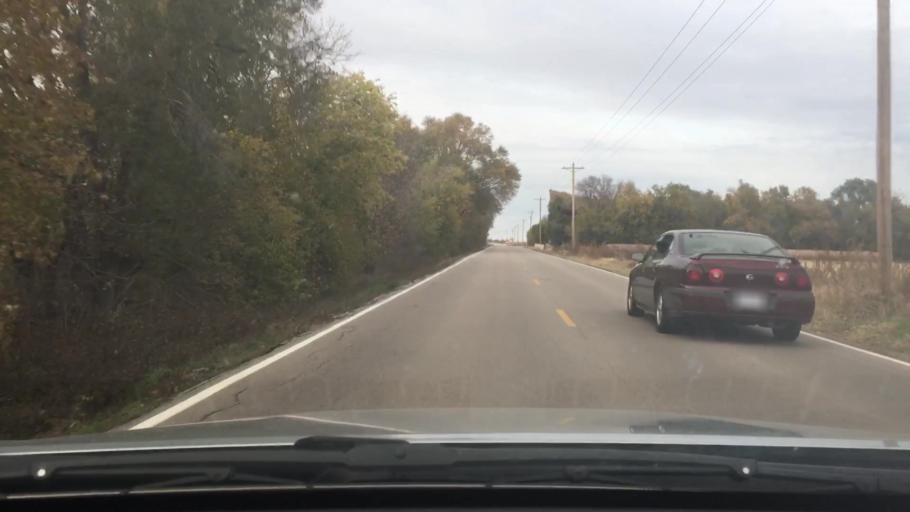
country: US
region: Kansas
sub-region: Sedgwick County
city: Maize
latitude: 37.7604
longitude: -97.4992
